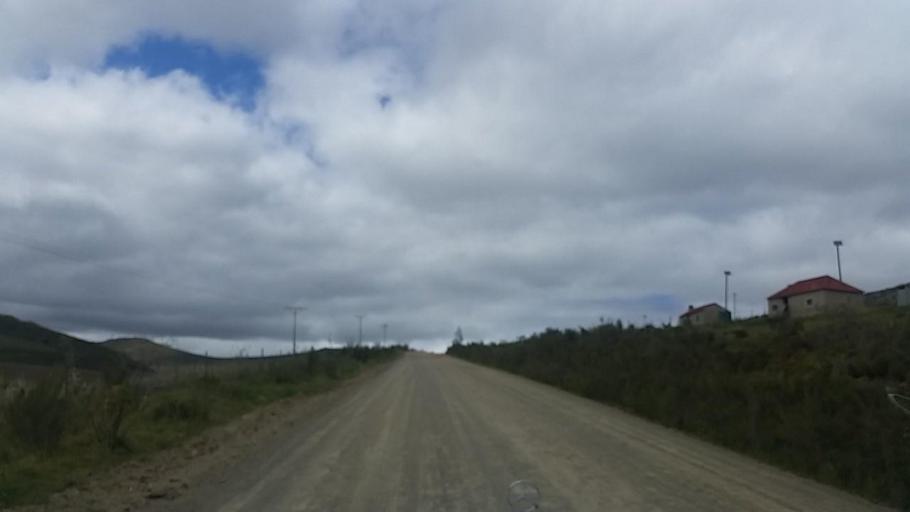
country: ZA
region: Western Cape
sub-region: Eden District Municipality
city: Knysna
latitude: -33.7369
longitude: 23.1673
